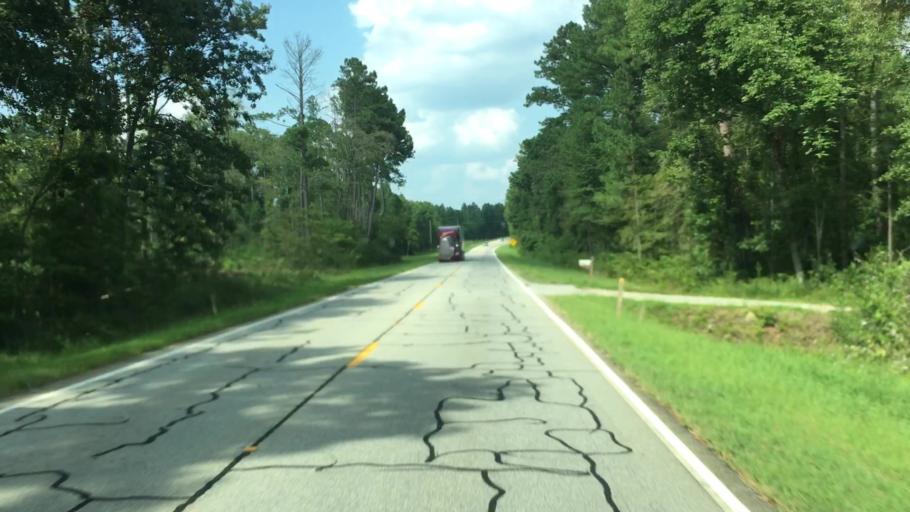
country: US
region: Georgia
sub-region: Butts County
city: Indian Springs
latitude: 33.1800
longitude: -83.7930
